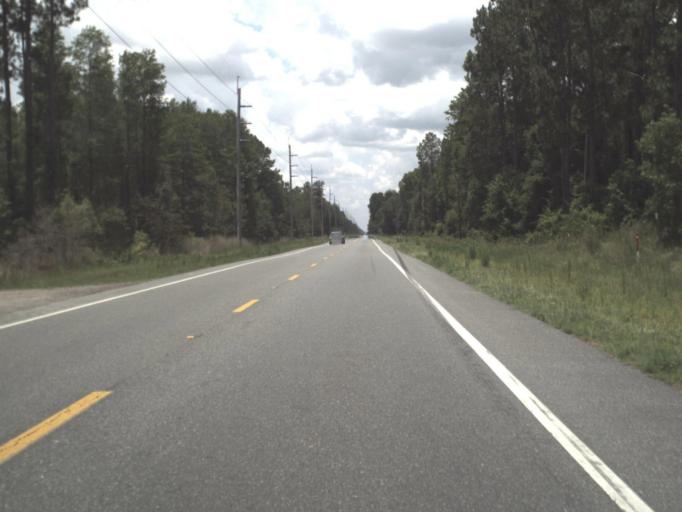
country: US
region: Florida
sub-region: Gilchrist County
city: Trenton
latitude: 29.6281
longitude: -82.7226
